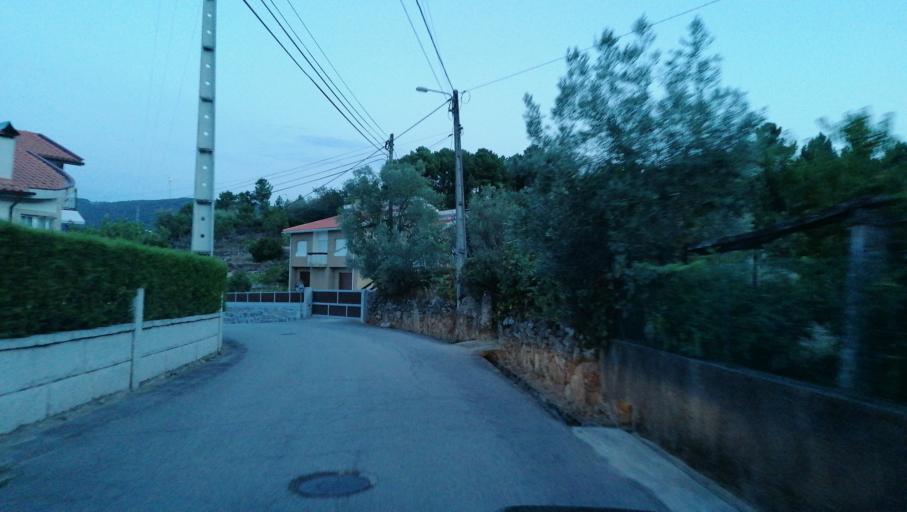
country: PT
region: Vila Real
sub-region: Vila Pouca de Aguiar
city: Vila Pouca de Aguiar
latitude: 41.5488
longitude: -7.6201
